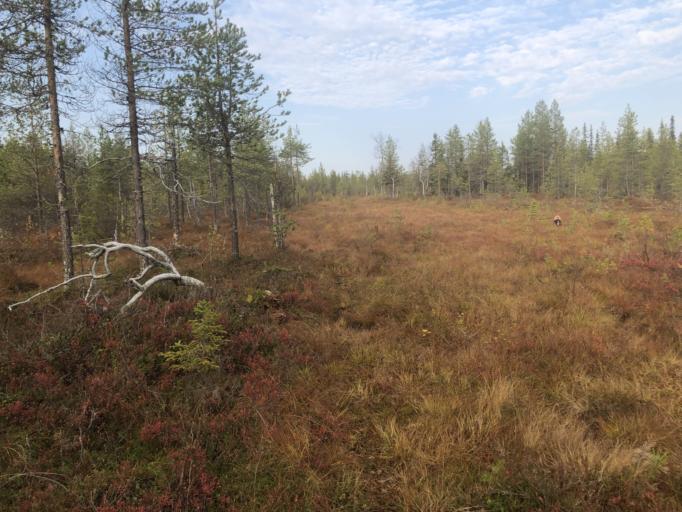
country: FI
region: Northern Ostrobothnia
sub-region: Koillismaa
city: Kuusamo
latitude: 66.5040
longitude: 29.4077
